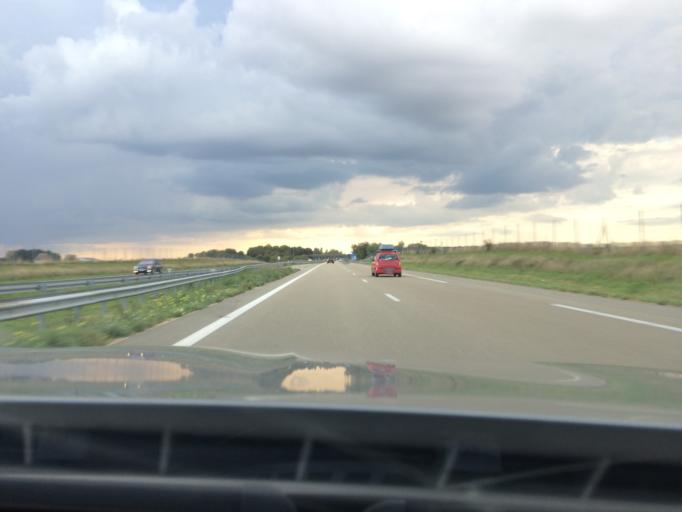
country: FR
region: Ile-de-France
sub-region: Departement de Seine-et-Marne
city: Egreville
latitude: 48.1814
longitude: 2.8393
